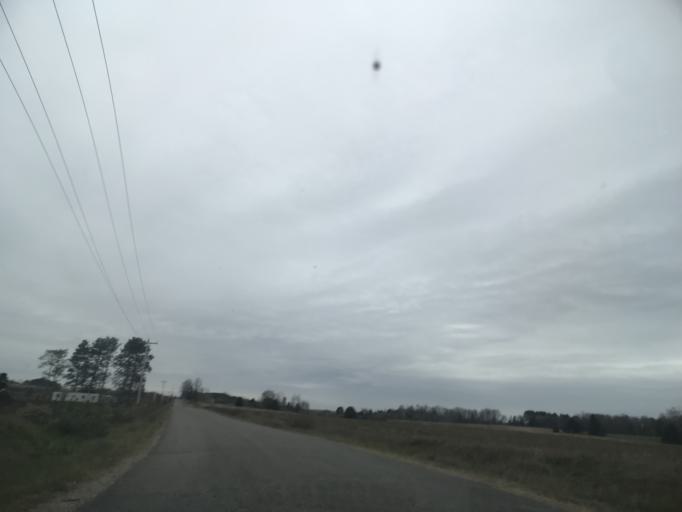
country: US
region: Wisconsin
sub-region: Menominee County
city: Legend Lake
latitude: 45.1813
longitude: -88.4553
